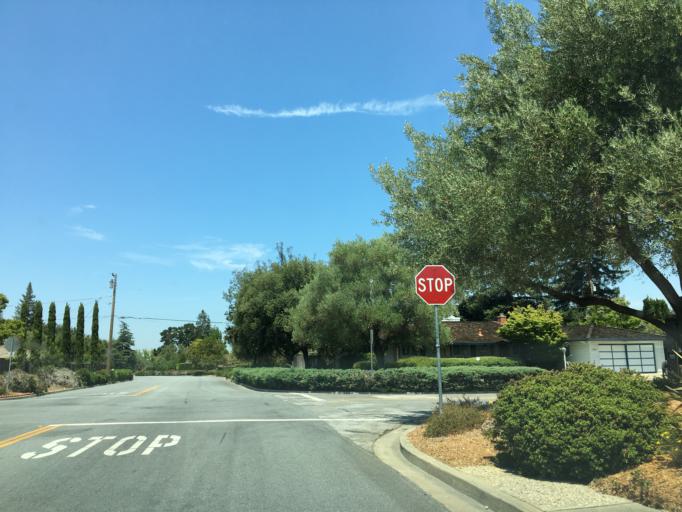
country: US
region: California
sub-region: Santa Clara County
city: Saratoga
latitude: 37.2871
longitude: -122.0120
